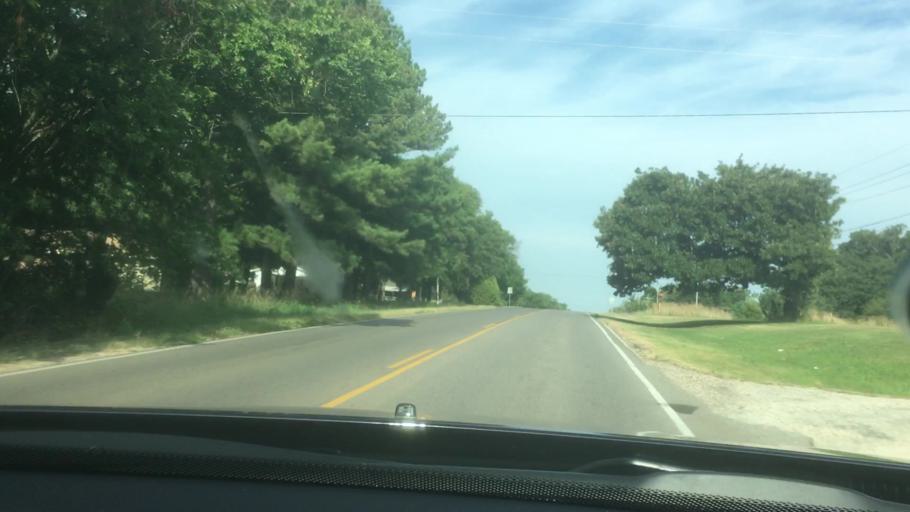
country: US
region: Oklahoma
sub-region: Pontotoc County
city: Ada
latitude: 34.7821
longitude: -96.7701
